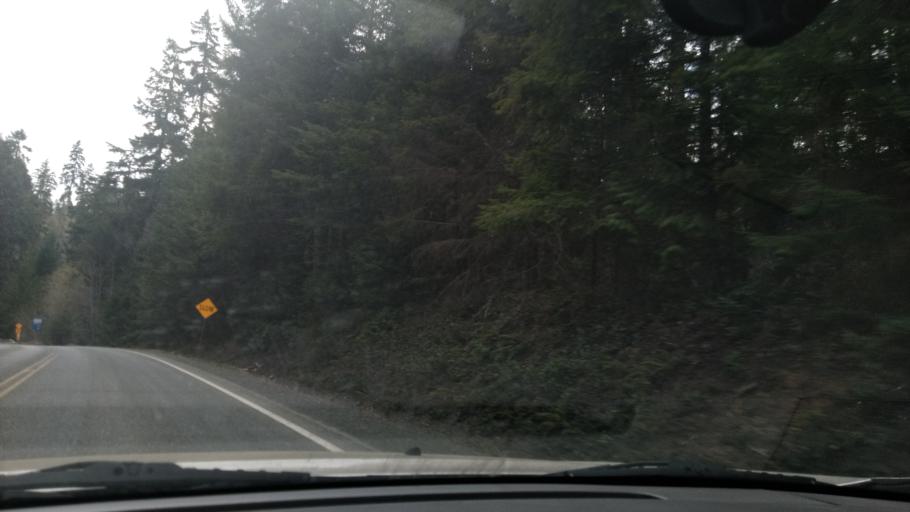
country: CA
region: British Columbia
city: Campbell River
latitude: 49.8515
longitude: -125.6248
